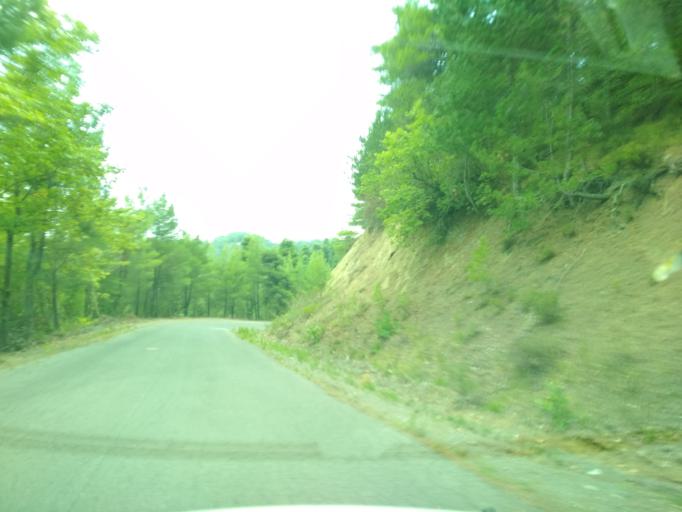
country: GR
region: Central Greece
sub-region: Nomos Evvoias
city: Roviai
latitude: 38.8526
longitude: 23.2831
